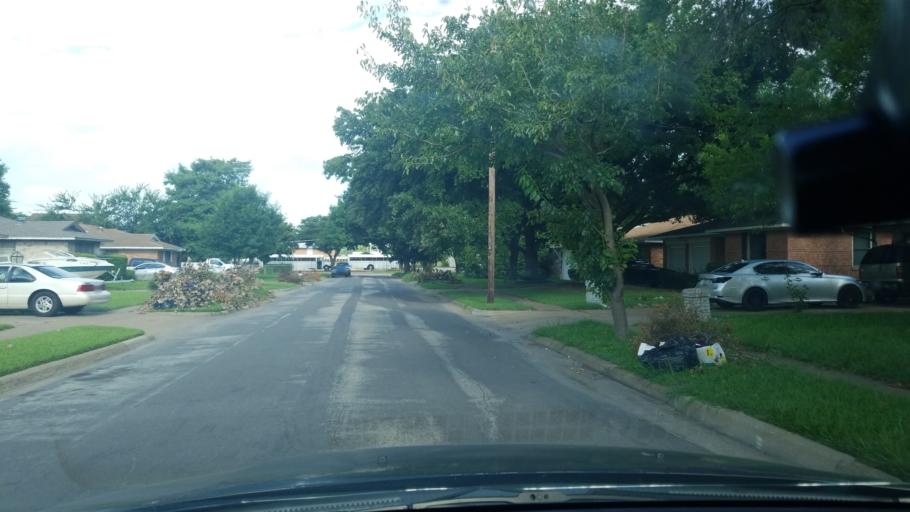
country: US
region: Texas
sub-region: Dallas County
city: Balch Springs
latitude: 32.7498
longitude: -96.6730
